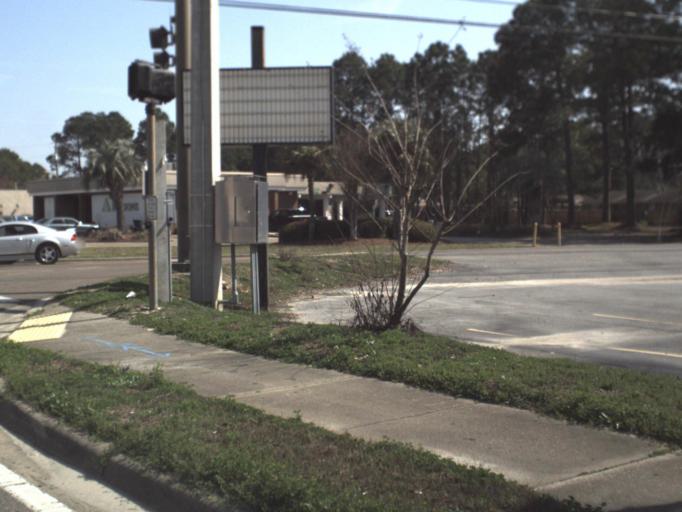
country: US
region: Florida
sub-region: Bay County
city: Pretty Bayou
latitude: 30.1896
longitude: -85.7011
